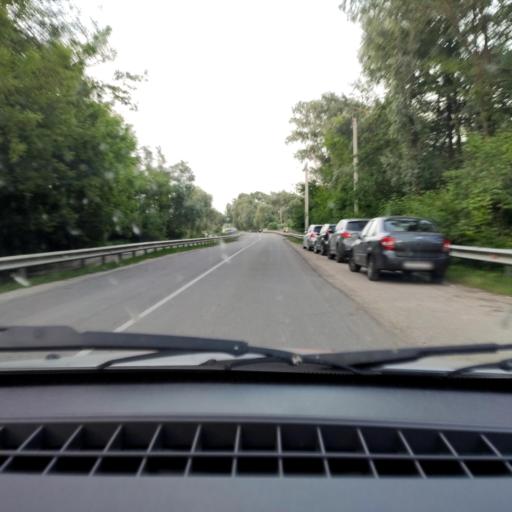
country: RU
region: Voronezj
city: Ramon'
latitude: 51.9494
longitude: 39.3814
